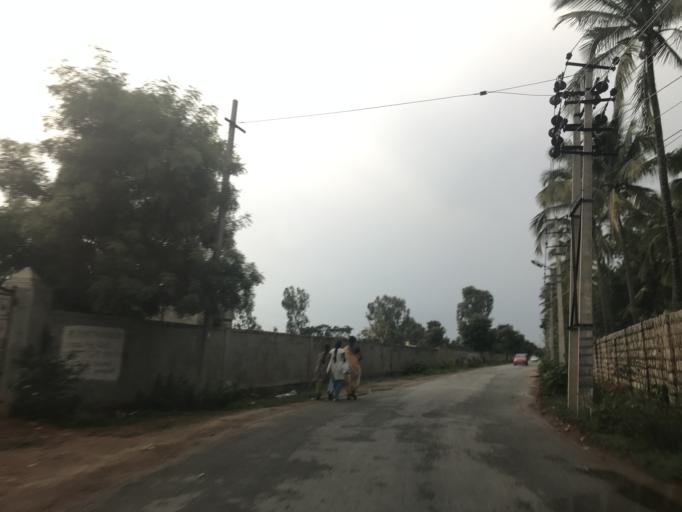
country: IN
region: Karnataka
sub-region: Bangalore Rural
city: Devanhalli
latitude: 13.1883
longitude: 77.6495
